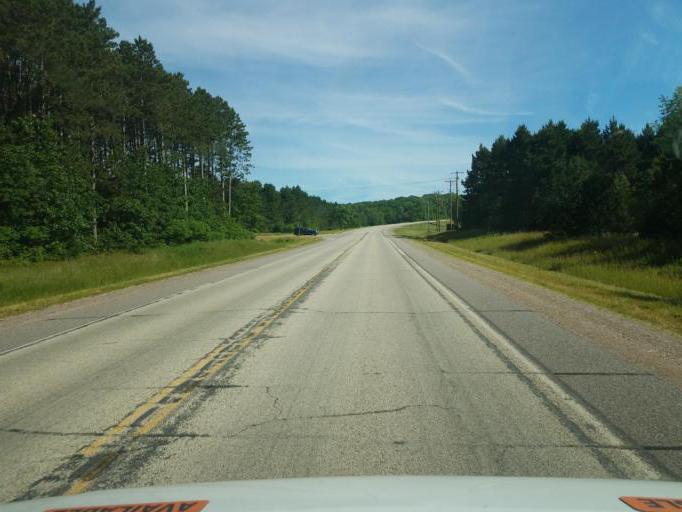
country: US
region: Wisconsin
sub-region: Sauk County
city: Lake Delton
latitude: 43.5786
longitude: -89.8233
